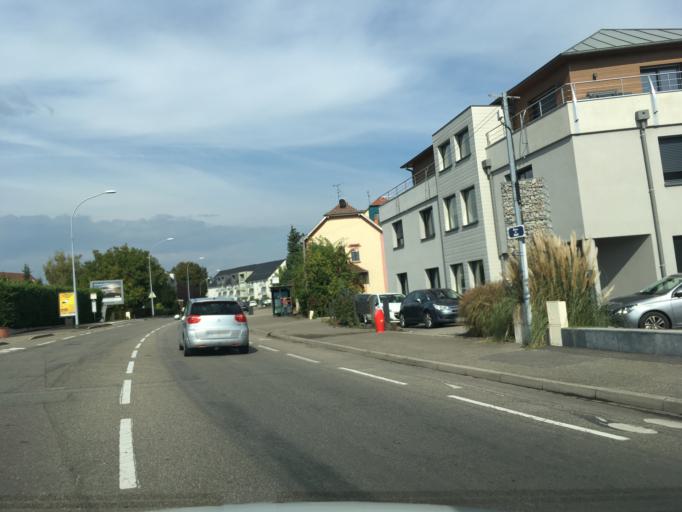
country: FR
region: Alsace
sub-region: Departement du Haut-Rhin
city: Colmar
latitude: 48.0627
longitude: 7.3623
